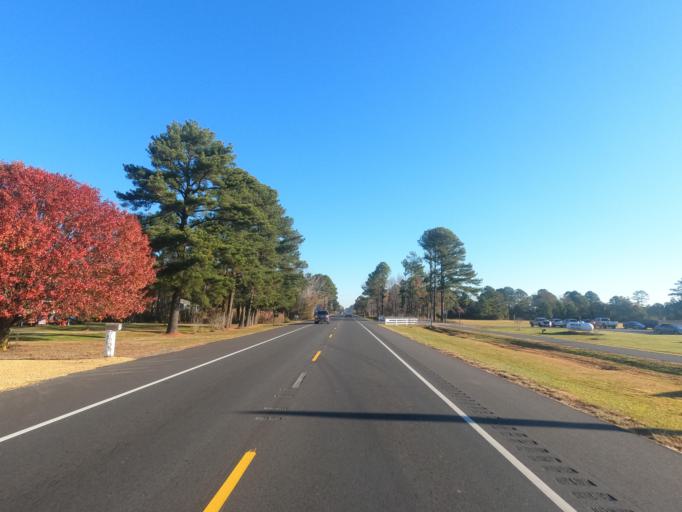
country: US
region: Maryland
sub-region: Somerset County
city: Crisfield
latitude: 38.0052
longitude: -75.8228
